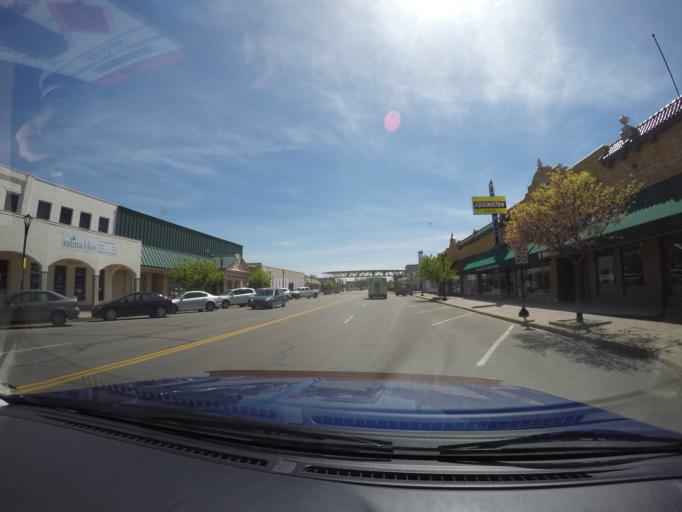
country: US
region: Kansas
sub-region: Saline County
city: Salina
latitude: 38.8381
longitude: -97.6091
